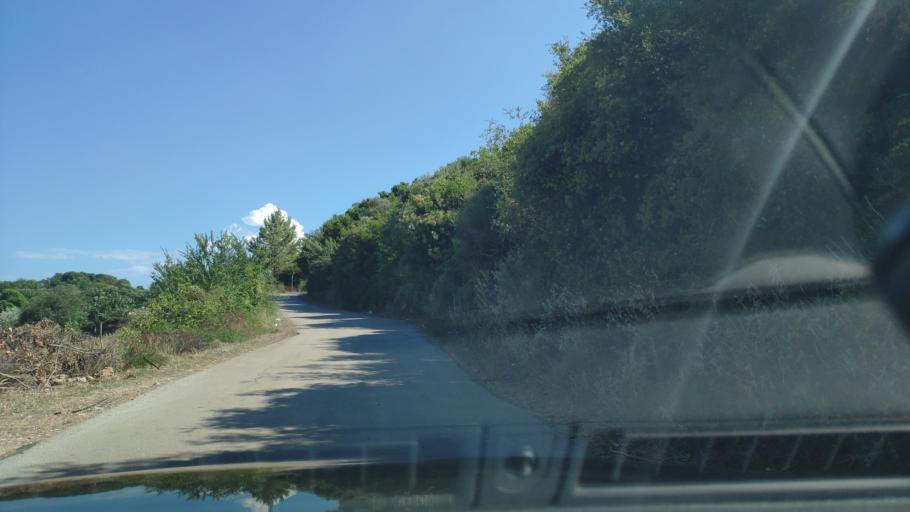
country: GR
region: West Greece
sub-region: Nomos Aitolias kai Akarnanias
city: Katouna
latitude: 38.7955
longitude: 21.1143
